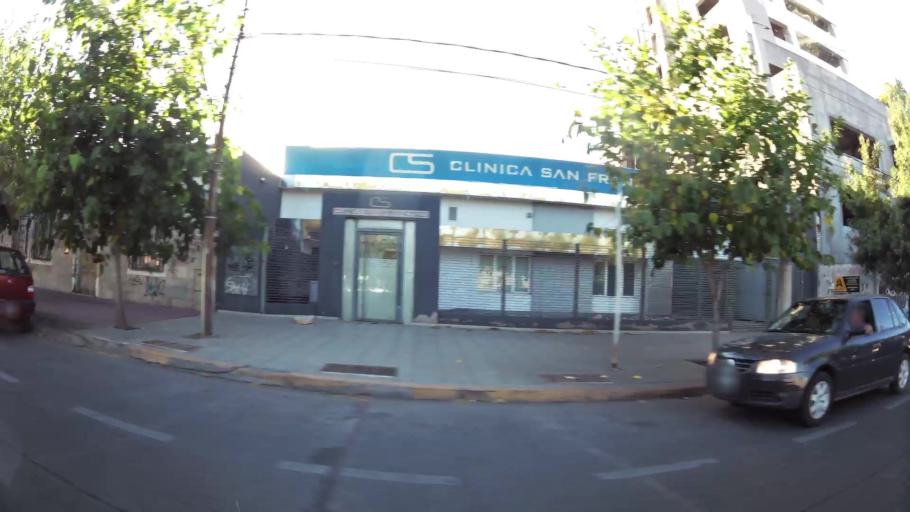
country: AR
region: Mendoza
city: Mendoza
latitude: -32.8819
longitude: -68.8465
